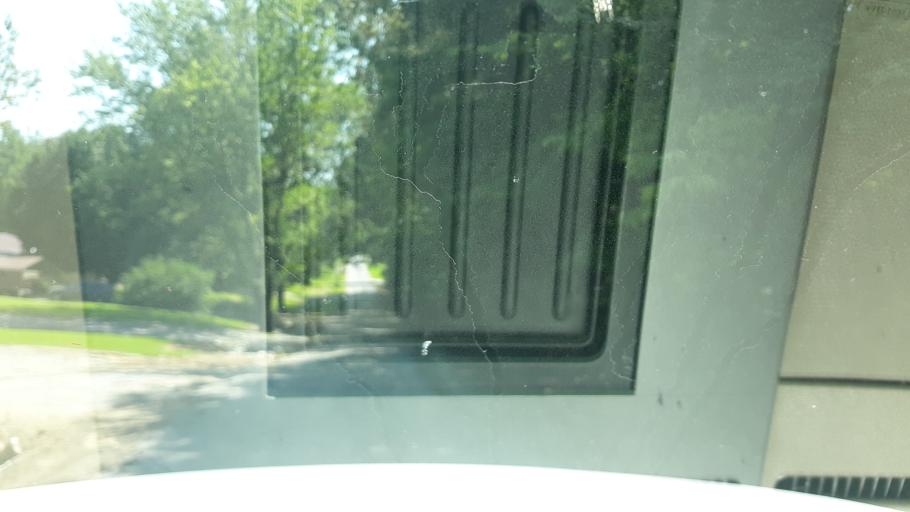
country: US
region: Illinois
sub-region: Saline County
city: Harrisburg
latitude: 37.8485
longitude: -88.6100
